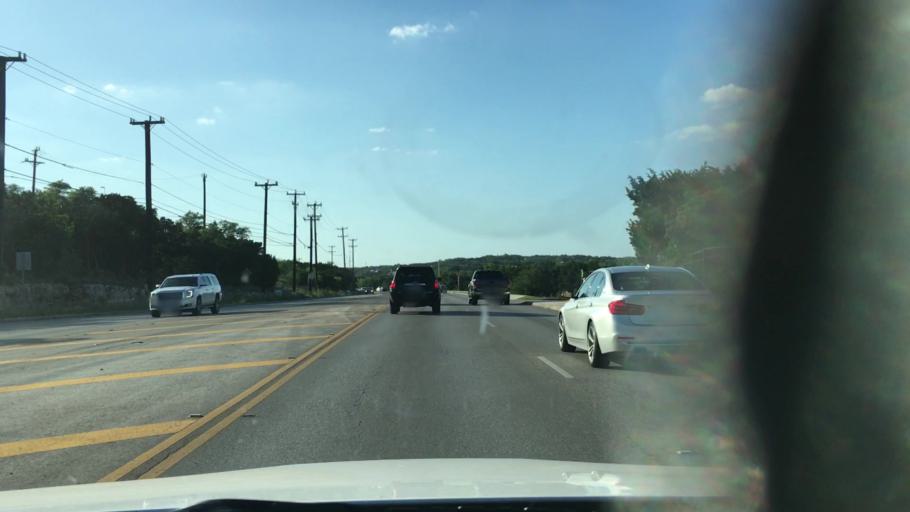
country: US
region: Texas
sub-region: Bexar County
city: Timberwood Park
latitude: 29.6570
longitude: -98.4322
